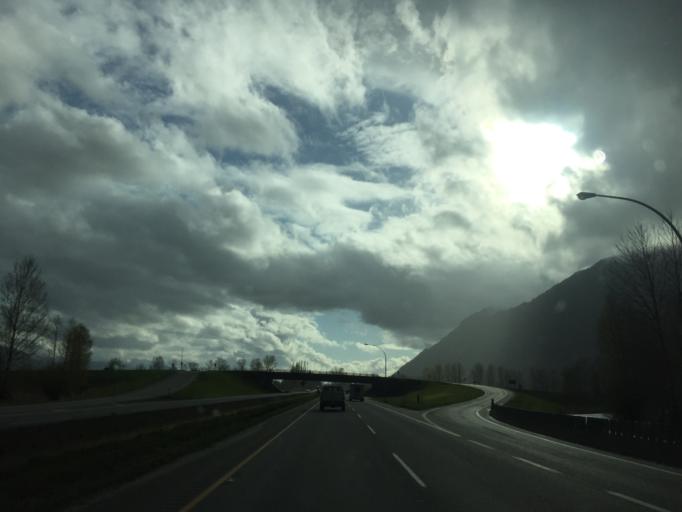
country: CA
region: British Columbia
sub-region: Fraser Valley Regional District
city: Chilliwack
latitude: 49.1317
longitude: -122.0793
